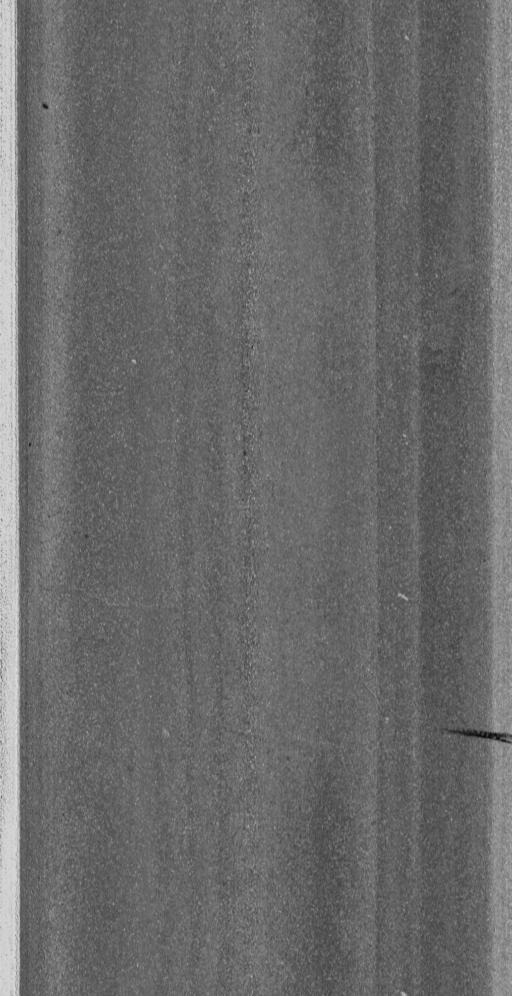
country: US
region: Vermont
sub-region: Chittenden County
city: South Burlington
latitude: 44.4540
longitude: -73.1815
